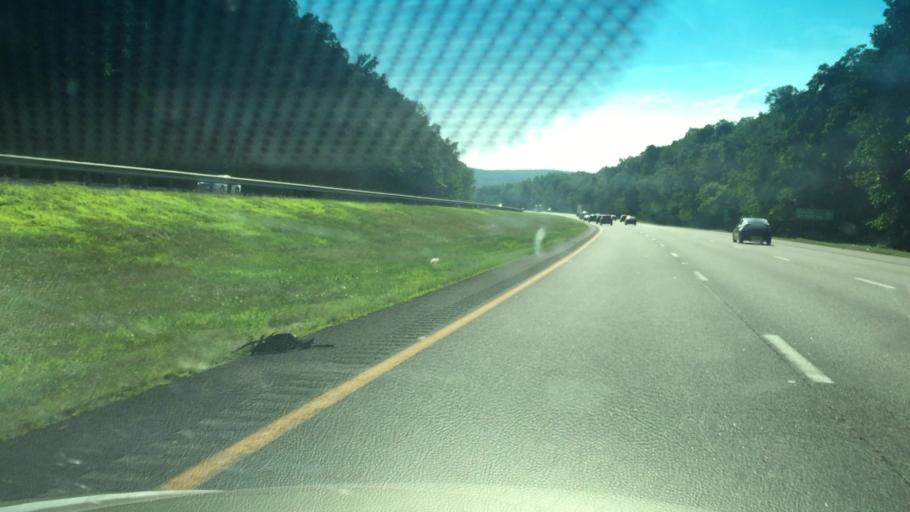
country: US
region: New Jersey
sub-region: Sussex County
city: Stanhope
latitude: 40.9124
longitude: -74.7407
